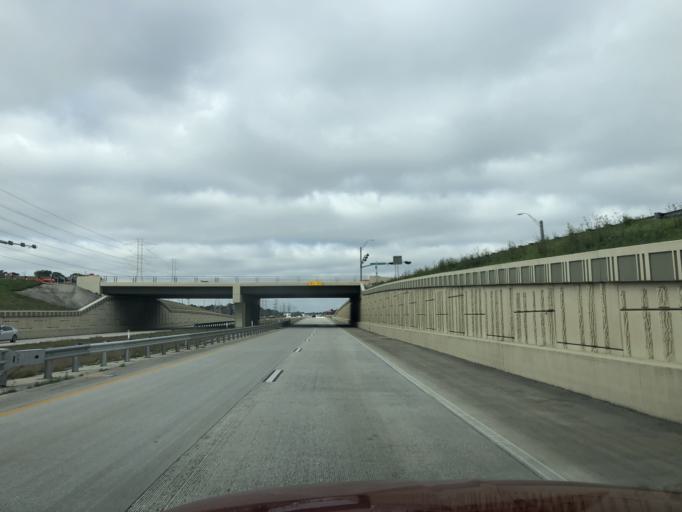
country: US
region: Texas
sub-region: Harris County
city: Spring
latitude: 30.0889
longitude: -95.4564
